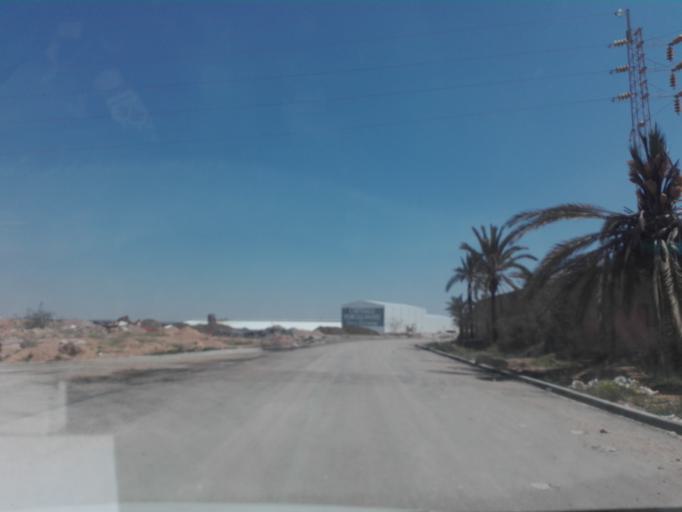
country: TN
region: Safaqis
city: Sfax
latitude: 34.7251
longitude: 10.5173
